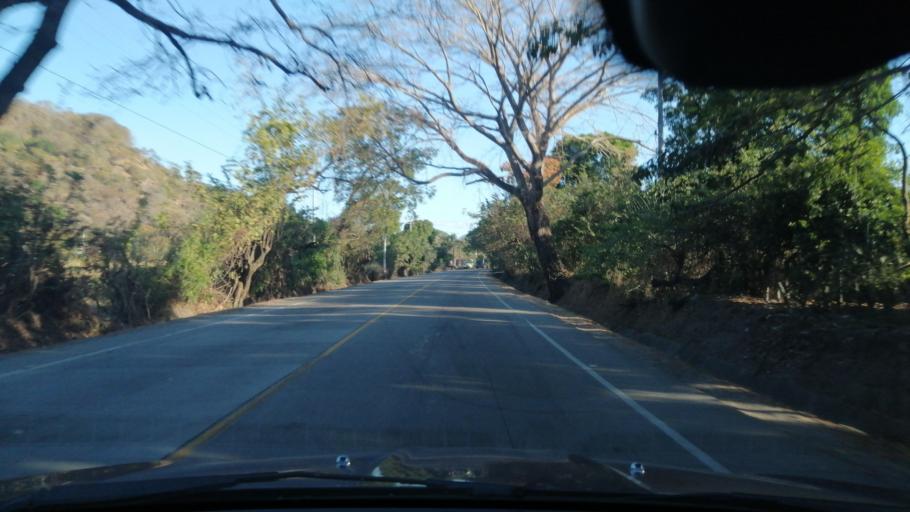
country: SV
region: Santa Ana
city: Texistepeque
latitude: 14.0859
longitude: -89.5000
